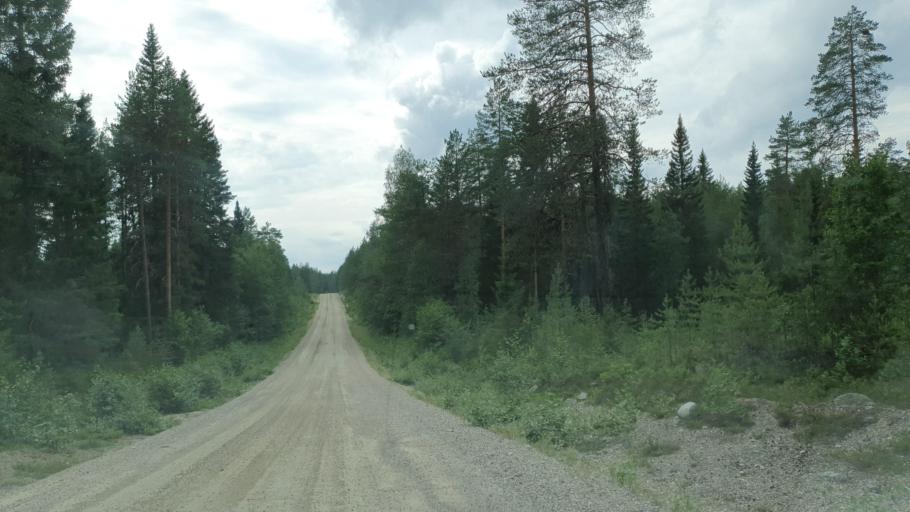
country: FI
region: Kainuu
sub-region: Kehys-Kainuu
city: Kuhmo
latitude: 64.7311
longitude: 29.7220
